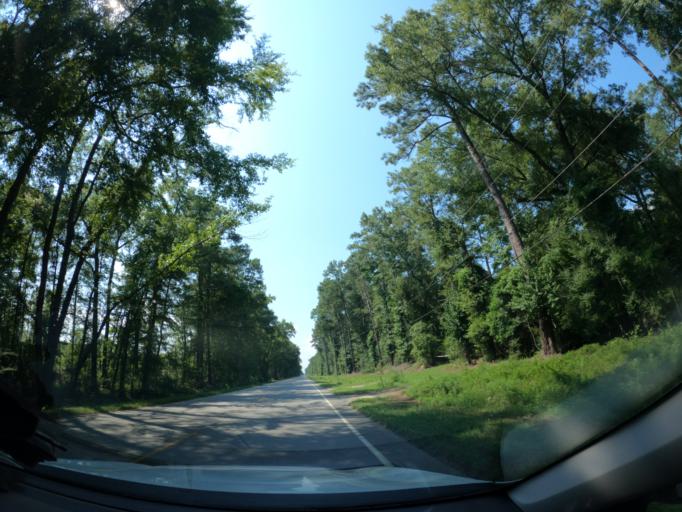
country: US
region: South Carolina
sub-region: Richland County
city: Hopkins
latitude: 33.9104
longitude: -80.9382
